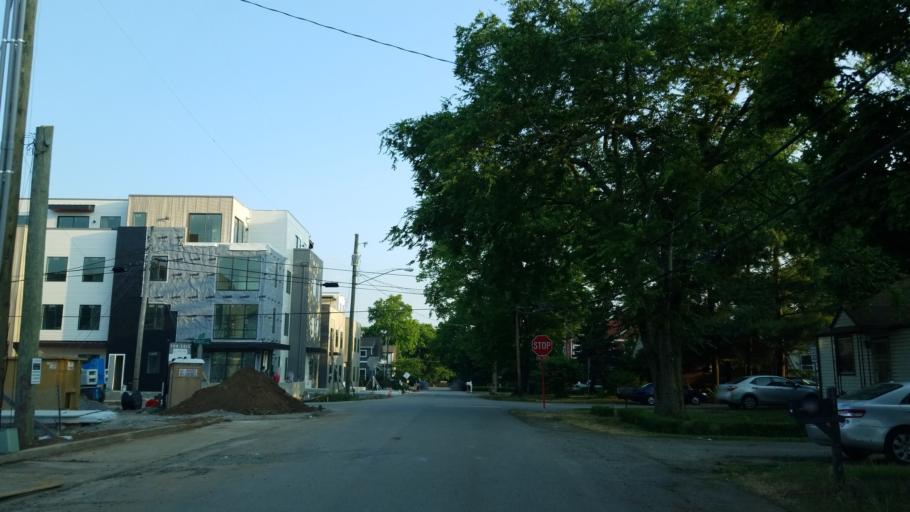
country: US
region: Tennessee
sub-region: Davidson County
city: Nashville
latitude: 36.1399
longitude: -86.7666
